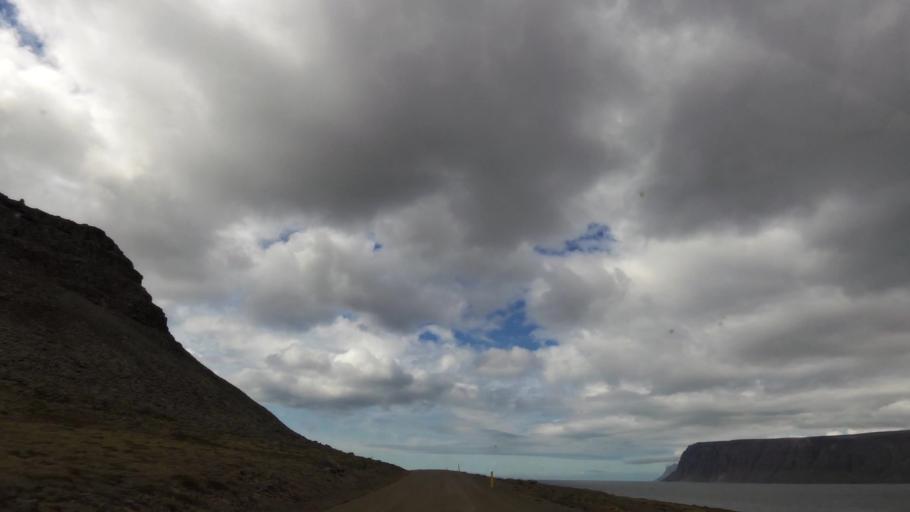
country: IS
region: West
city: Olafsvik
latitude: 65.5736
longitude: -24.0645
